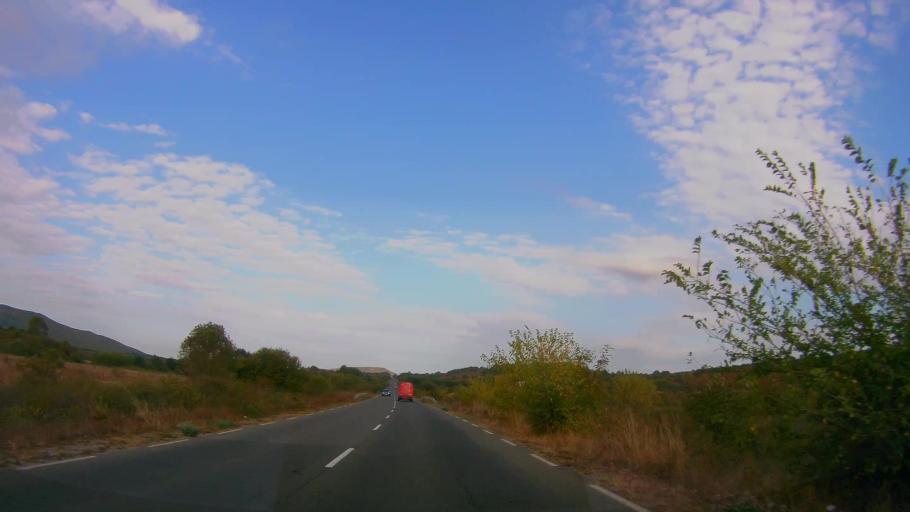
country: BG
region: Burgas
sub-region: Obshtina Sozopol
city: Sozopol
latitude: 42.3640
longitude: 27.6968
